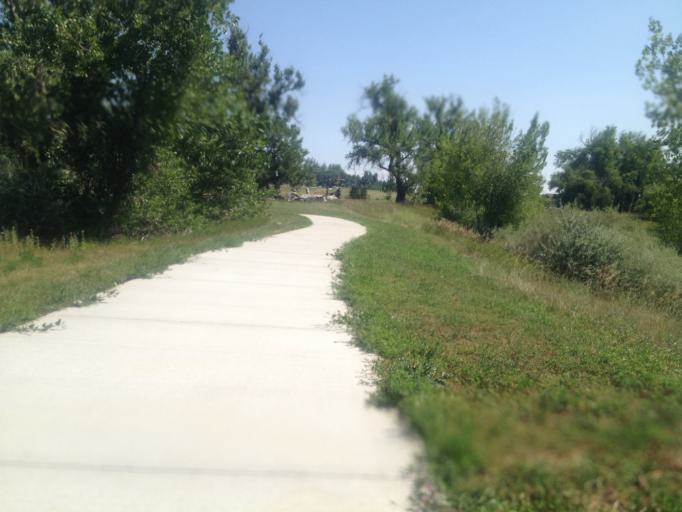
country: US
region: Colorado
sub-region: Boulder County
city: Louisville
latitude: 39.9977
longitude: -105.1299
